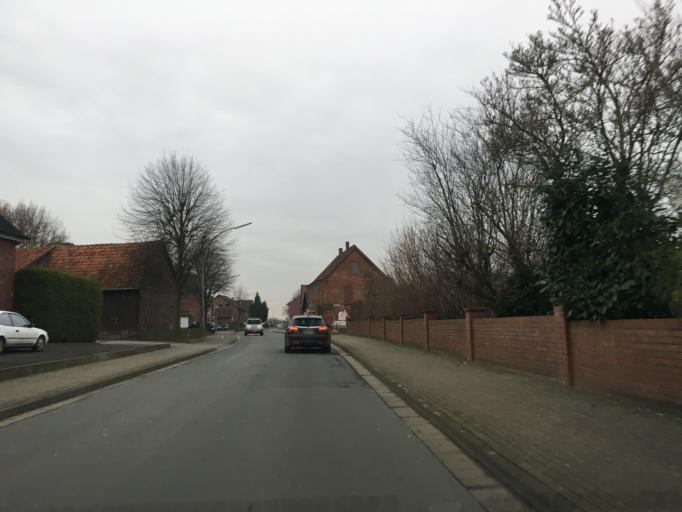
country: DE
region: North Rhine-Westphalia
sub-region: Regierungsbezirk Munster
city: Nordkirchen
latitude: 51.7347
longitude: 7.5186
